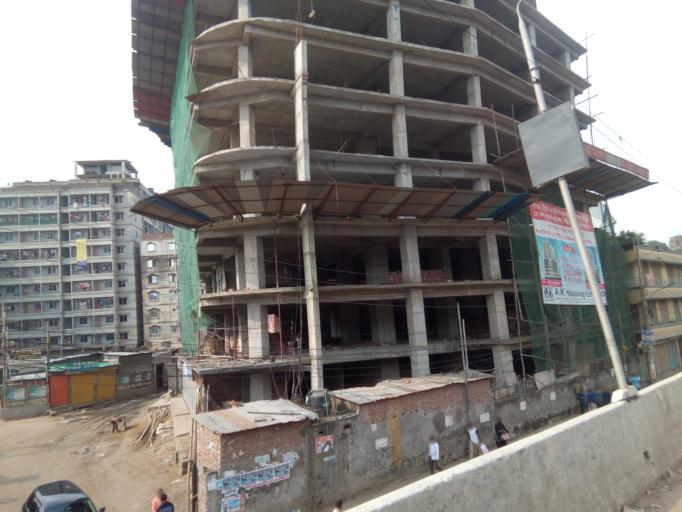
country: BD
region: Dhaka
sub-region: Dhaka
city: Dhaka
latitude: 23.7133
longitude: 90.4041
